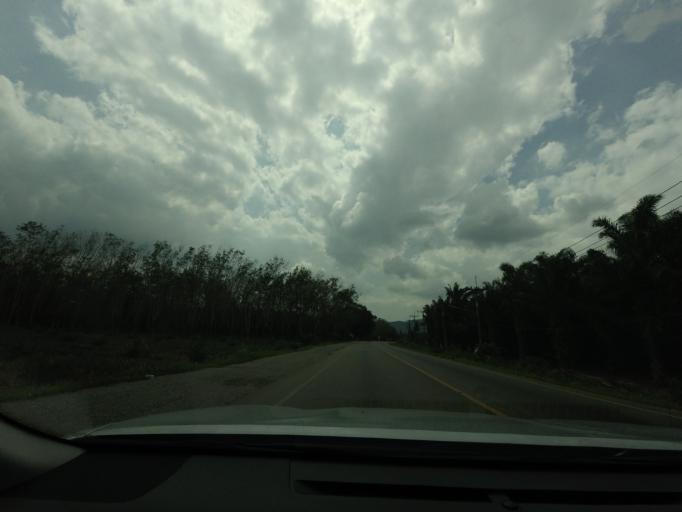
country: TH
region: Phangnga
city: Ban Ao Nang
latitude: 8.1263
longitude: 98.8057
